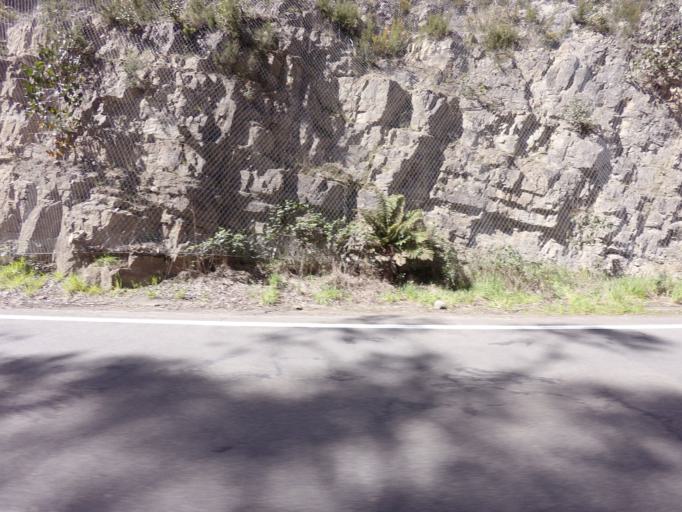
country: AU
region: Tasmania
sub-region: Derwent Valley
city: New Norfolk
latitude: -42.6841
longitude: 146.7274
